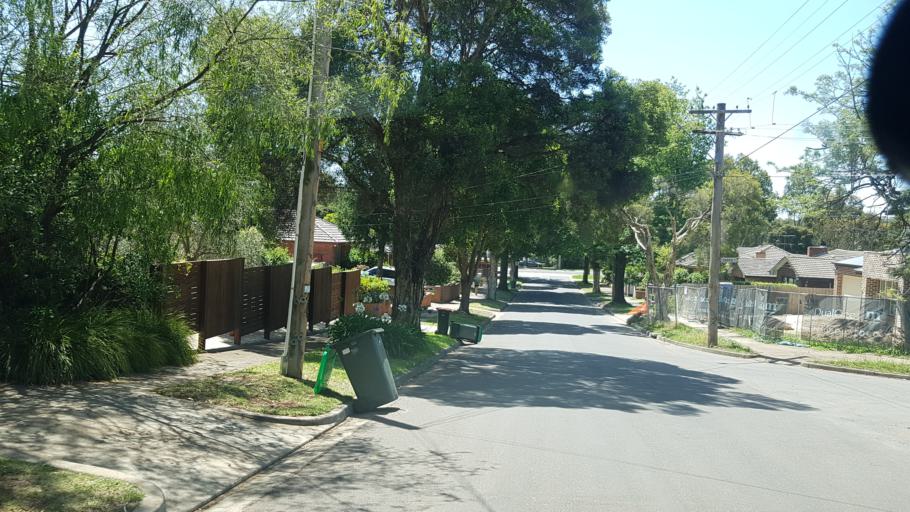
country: AU
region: Victoria
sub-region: Banyule
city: Viewbank
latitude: -37.7573
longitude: 145.0996
